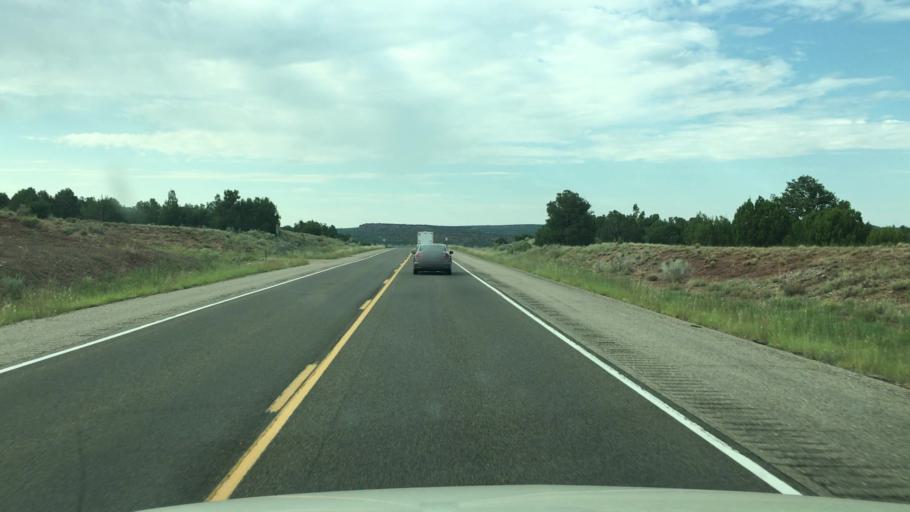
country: US
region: New Mexico
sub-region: Santa Fe County
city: Eldorado at Santa Fe
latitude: 35.2600
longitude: -105.8088
